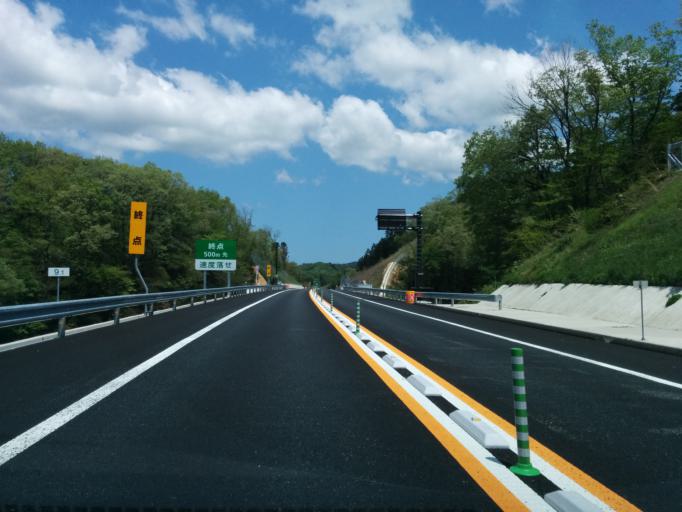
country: JP
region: Kyoto
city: Miyazu
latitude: 35.5680
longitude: 135.1208
